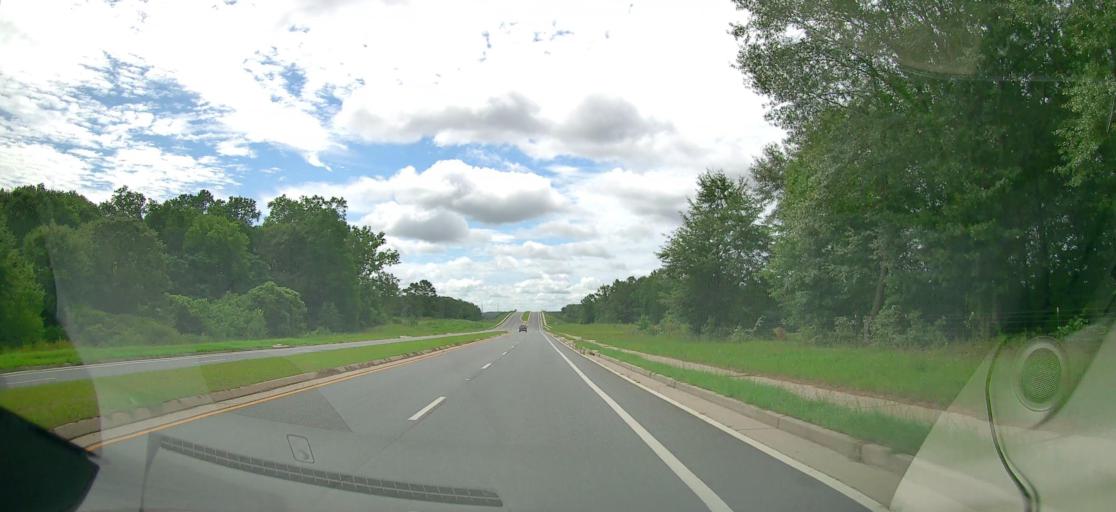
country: US
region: Georgia
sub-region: Houston County
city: Centerville
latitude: 32.6949
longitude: -83.6891
